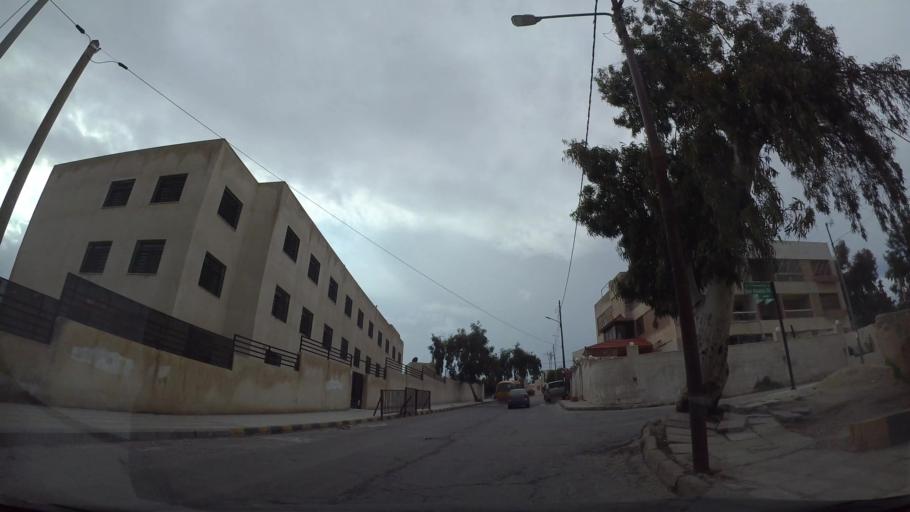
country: JO
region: Amman
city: Amman
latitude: 32.0036
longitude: 35.9478
